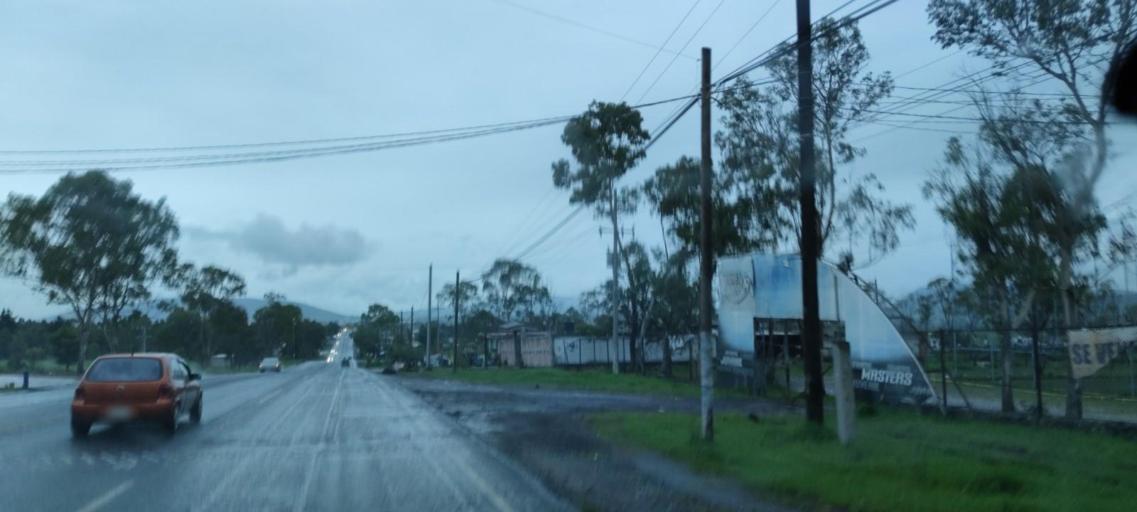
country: MX
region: Mexico
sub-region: Jilotepec
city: Doxhicho
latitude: 19.9431
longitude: -99.5598
